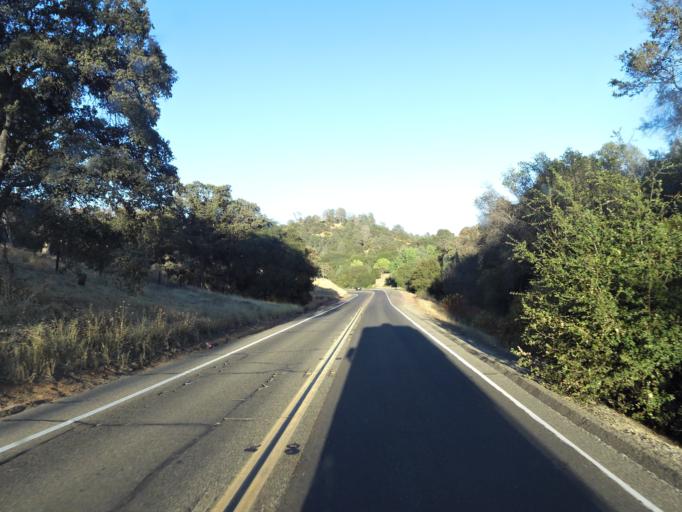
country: US
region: California
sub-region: Mariposa County
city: Mariposa
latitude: 37.4716
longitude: -119.9676
